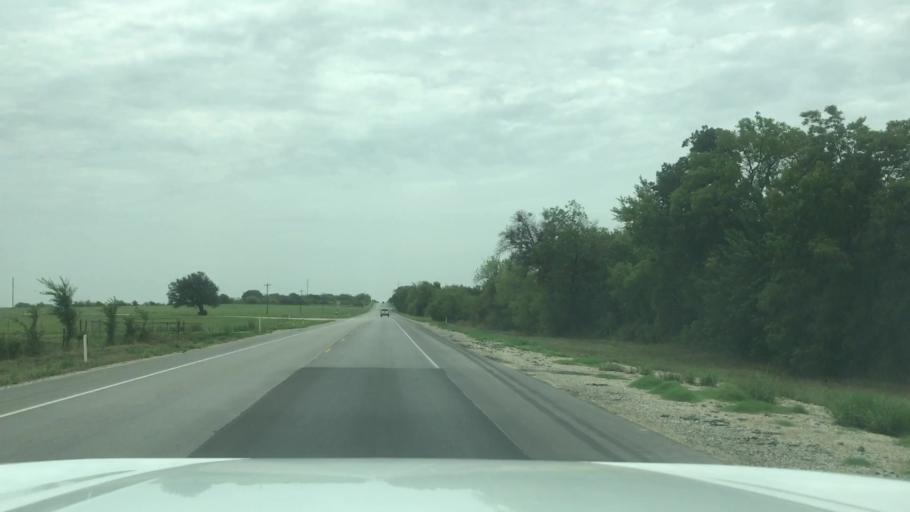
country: US
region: Texas
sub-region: Erath County
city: Dublin
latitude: 32.0909
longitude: -98.2641
